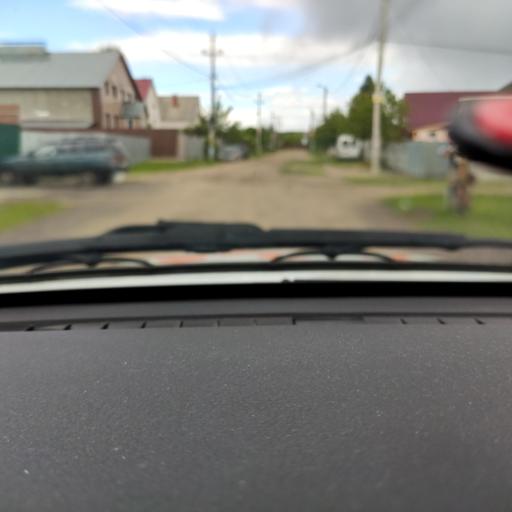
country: RU
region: Voronezj
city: Podgornoye
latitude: 51.7426
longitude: 39.1539
